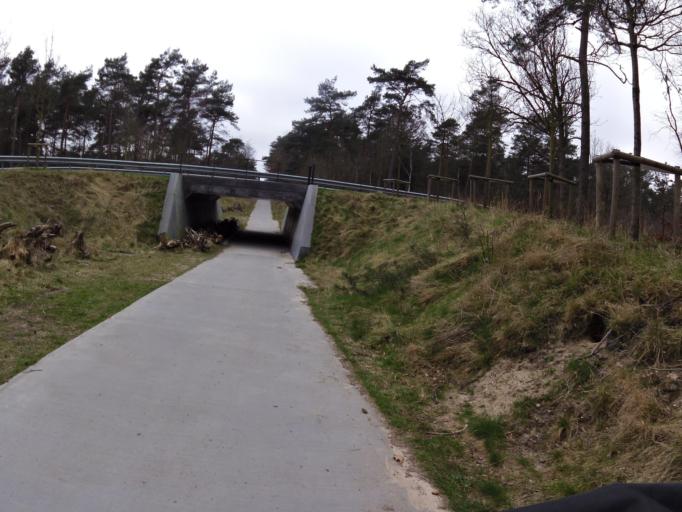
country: NL
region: Drenthe
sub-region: Gemeente Westerveld
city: Dwingeloo
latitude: 52.9466
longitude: 6.3183
